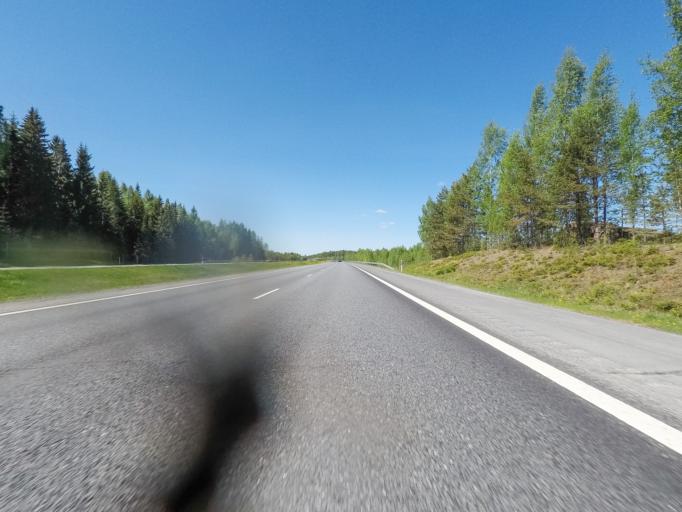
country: FI
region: Haeme
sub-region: Haemeenlinna
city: Kalvola
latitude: 61.1209
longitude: 24.1249
